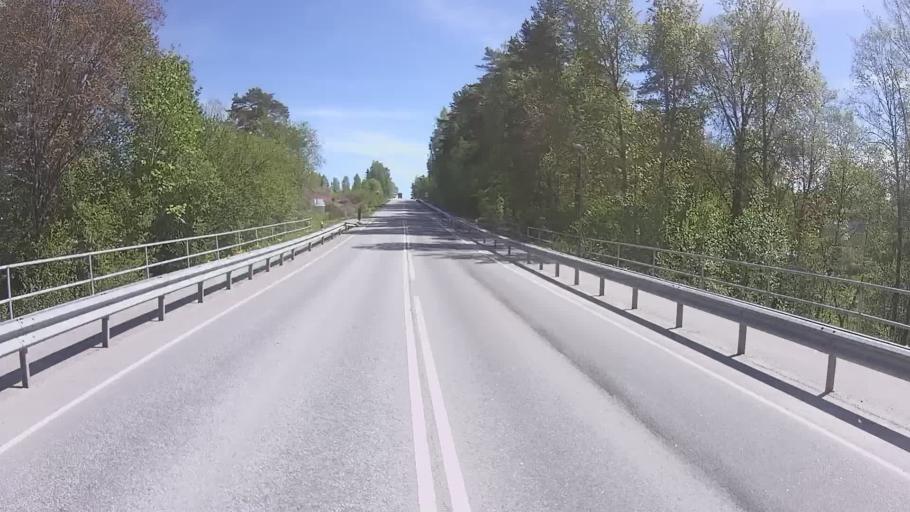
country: EE
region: Vorumaa
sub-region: Voru linn
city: Voru
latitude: 57.8131
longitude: 27.0452
